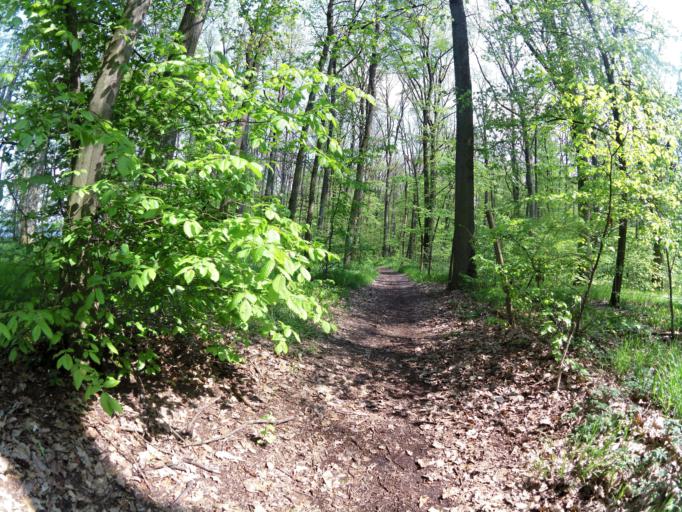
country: DE
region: Bavaria
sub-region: Regierungsbezirk Unterfranken
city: Sommerhausen
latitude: 49.7067
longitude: 10.0603
